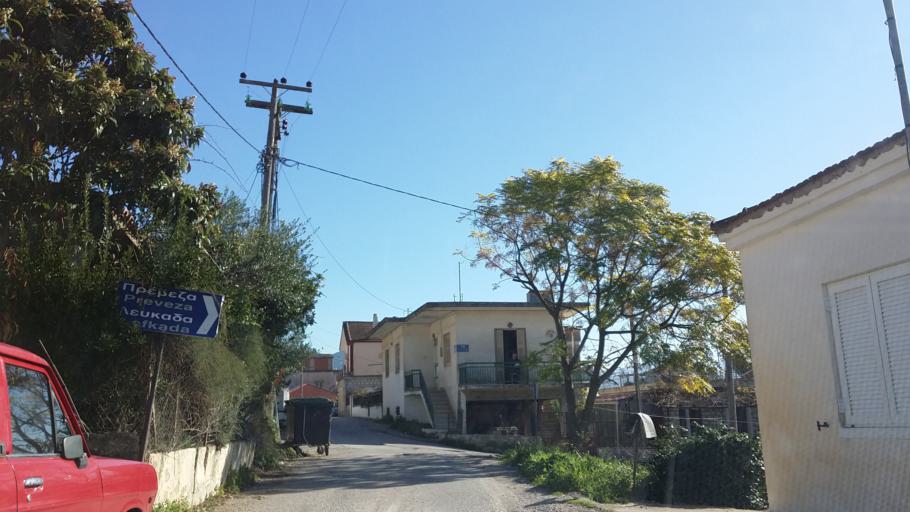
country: GR
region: West Greece
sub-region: Nomos Aitolias kai Akarnanias
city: Vonitsa
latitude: 38.9187
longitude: 20.8852
